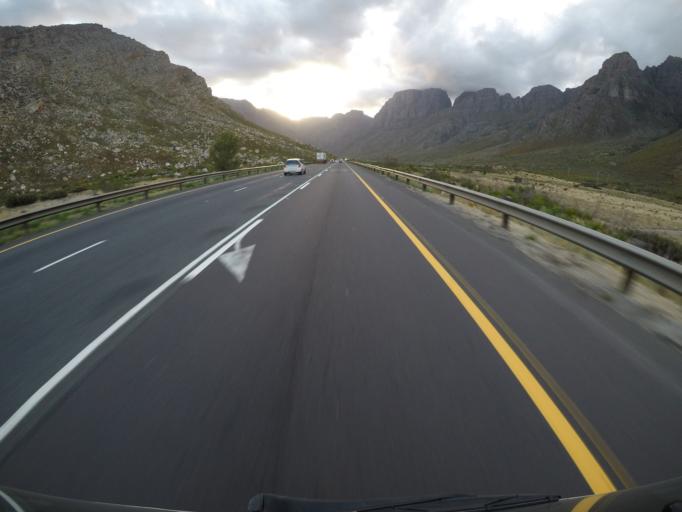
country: ZA
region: Western Cape
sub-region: Cape Winelands District Municipality
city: Worcester
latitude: -33.7032
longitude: 19.2343
